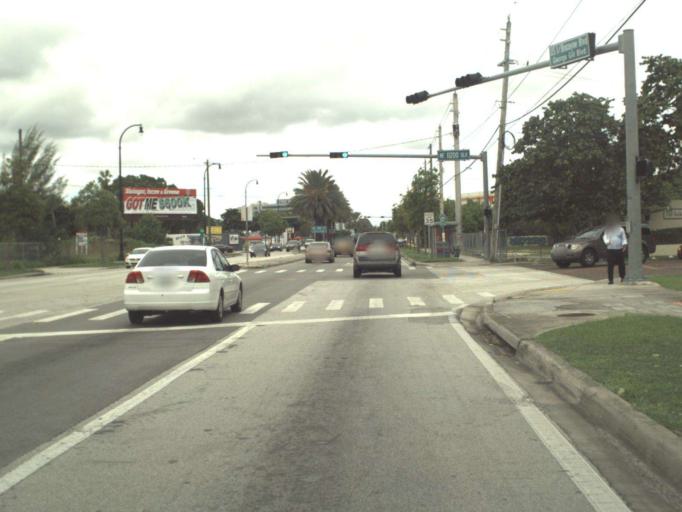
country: US
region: Florida
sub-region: Miami-Dade County
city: Biscayne Park
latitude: 25.8793
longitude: -80.1674
